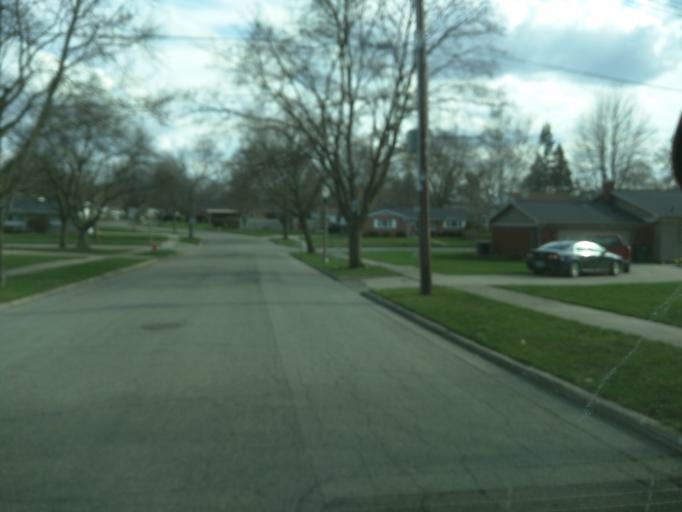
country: US
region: Michigan
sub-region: Ingham County
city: Edgemont Park
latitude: 42.7601
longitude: -84.5987
